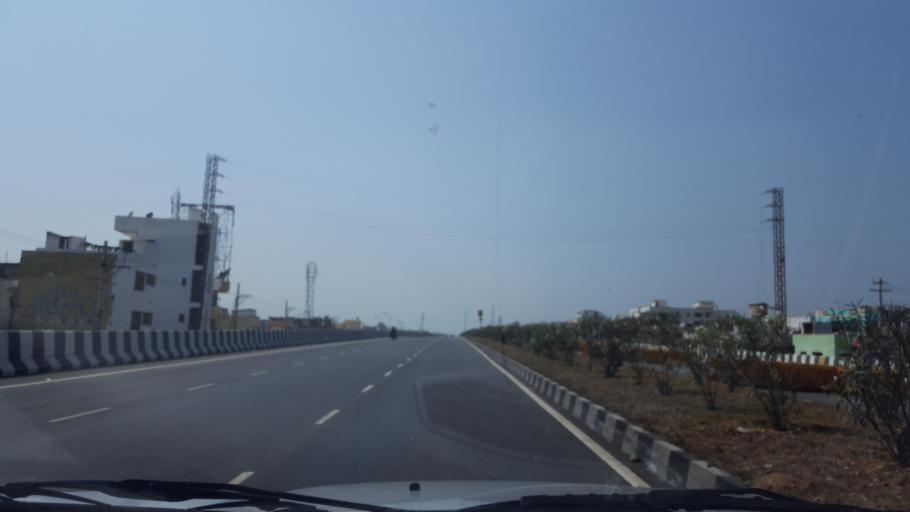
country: IN
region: Andhra Pradesh
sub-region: Guntur
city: Chilakalurupet
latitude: 15.9868
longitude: 80.1043
